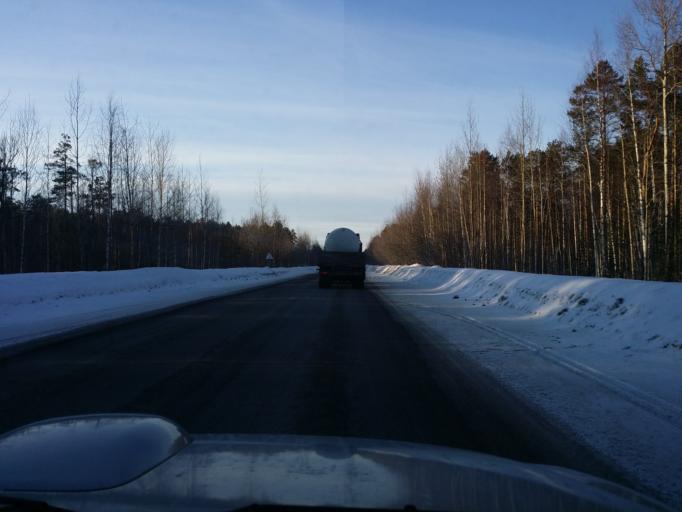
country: RU
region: Khanty-Mansiyskiy Avtonomnyy Okrug
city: Izluchinsk
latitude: 60.9395
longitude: 76.8612
